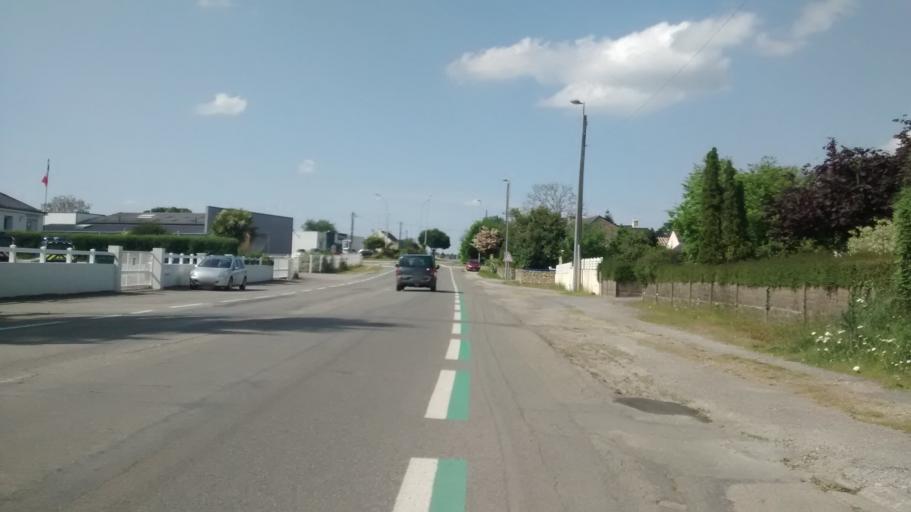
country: FR
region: Brittany
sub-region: Departement du Morbihan
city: Questembert
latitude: 47.6667
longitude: -2.4498
